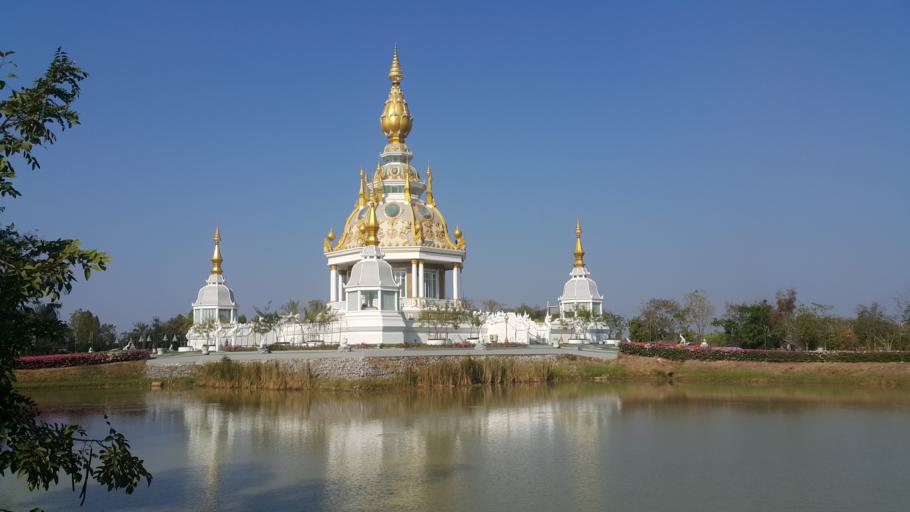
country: TH
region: Khon Kaen
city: Khon Kaen
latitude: 16.4106
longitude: 102.8835
